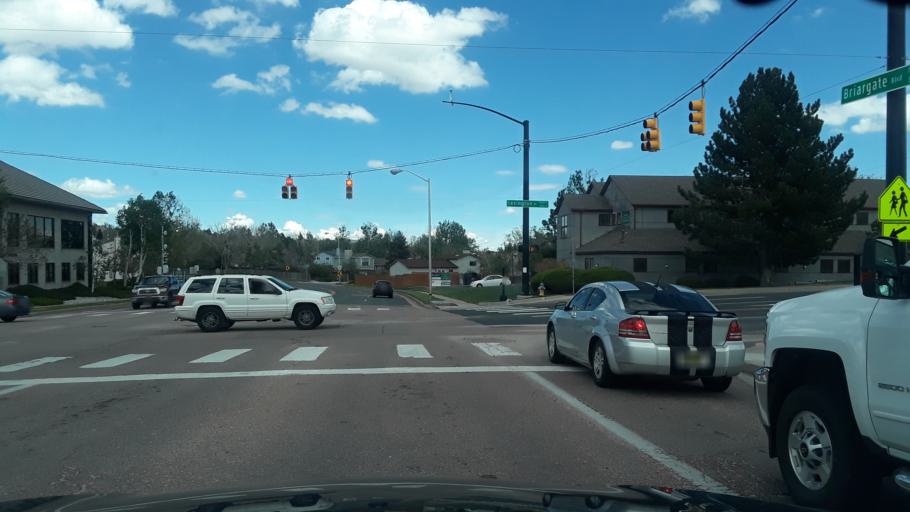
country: US
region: Colorado
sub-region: El Paso County
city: Black Forest
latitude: 38.9417
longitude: -104.7634
